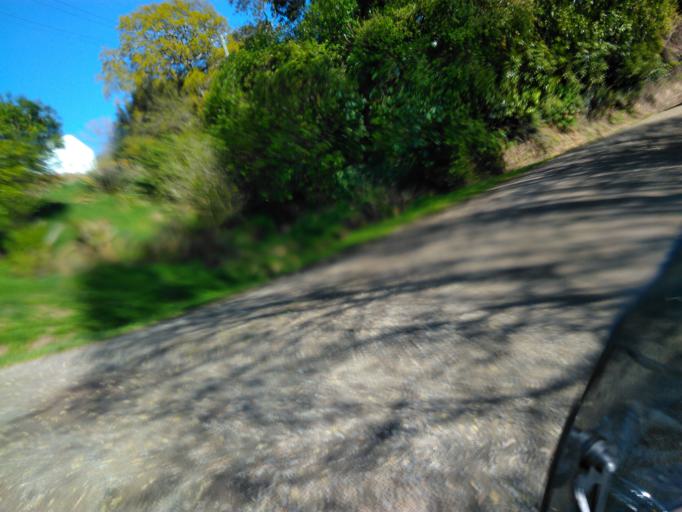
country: NZ
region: Bay of Plenty
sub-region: Opotiki District
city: Opotiki
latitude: -38.3725
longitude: 177.6036
